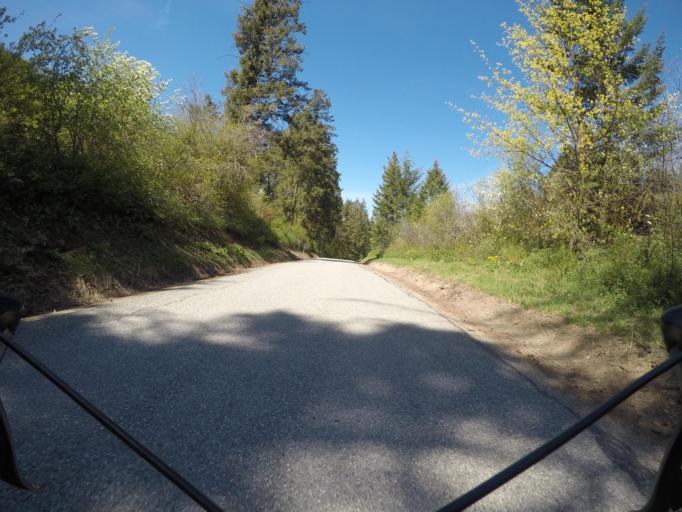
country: US
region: Washington
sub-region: Chelan County
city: Leavenworth
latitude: 47.5477
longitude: -120.5796
